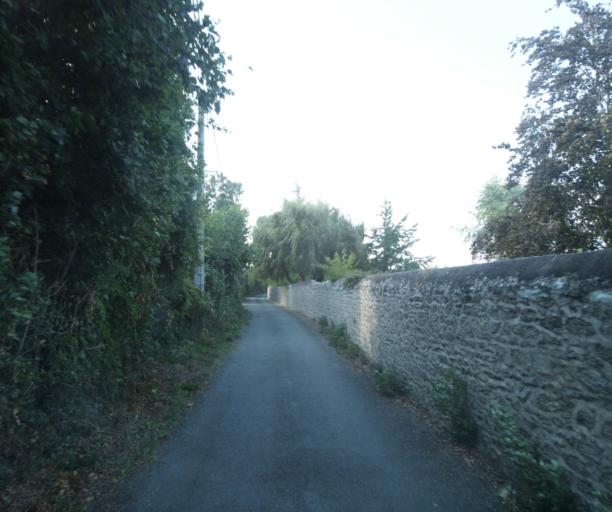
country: FR
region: Rhone-Alpes
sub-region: Departement du Rhone
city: Lentilly
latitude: 45.8302
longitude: 4.6710
